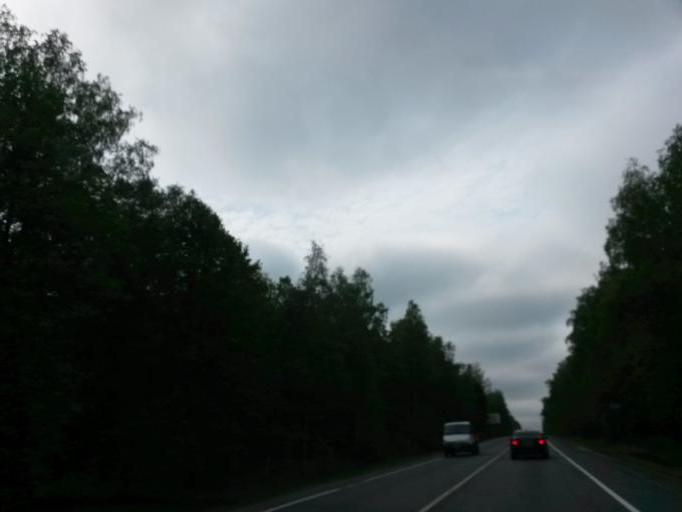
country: RU
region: Moskovskaya
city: Klimovsk
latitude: 55.3314
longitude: 37.6409
